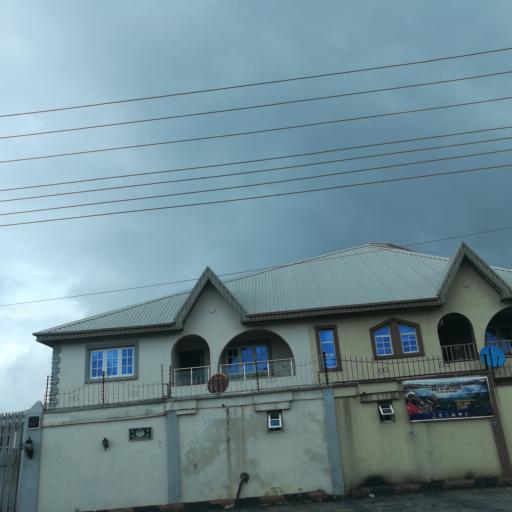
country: NG
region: Lagos
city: Ikoyi
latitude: 6.4400
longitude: 3.4641
